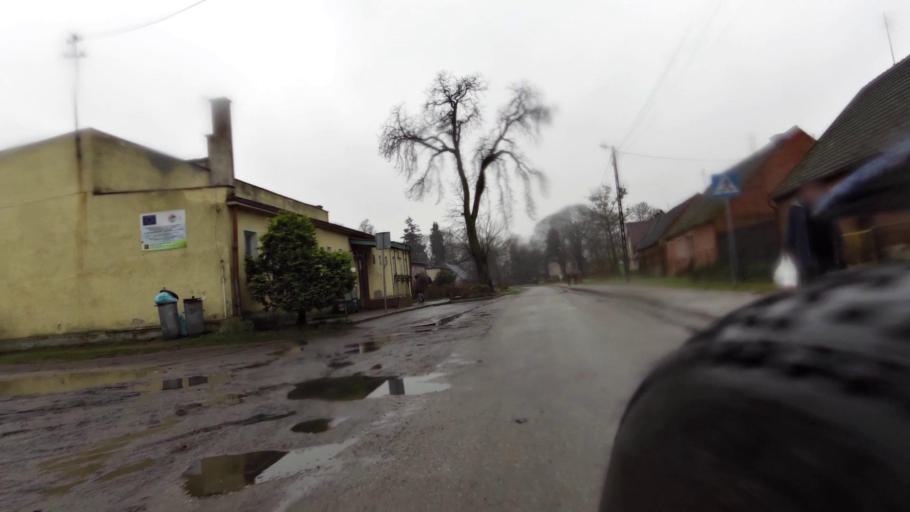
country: PL
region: West Pomeranian Voivodeship
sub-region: Powiat drawski
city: Zlocieniec
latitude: 53.5434
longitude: 15.9587
